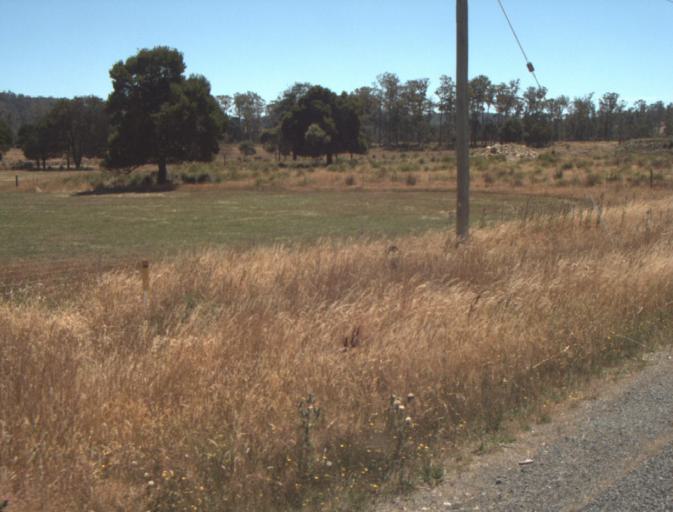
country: AU
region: Tasmania
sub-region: Launceston
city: Newstead
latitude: -41.3631
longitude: 147.3345
